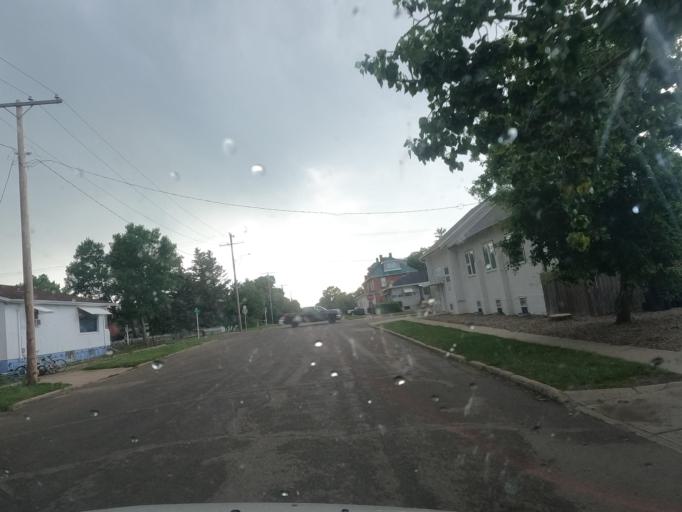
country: CA
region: Saskatchewan
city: Weyburn
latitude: 49.6574
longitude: -103.8540
